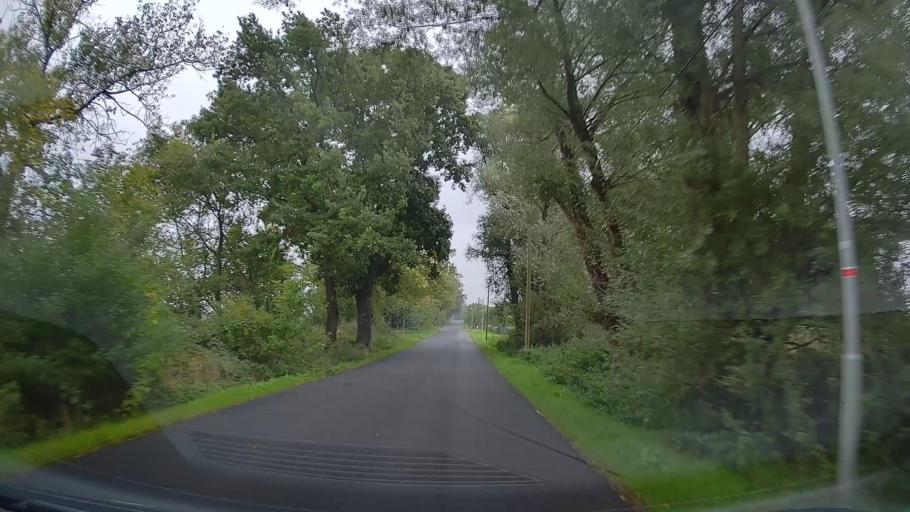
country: DE
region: Mecklenburg-Vorpommern
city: Hornstorf
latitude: 53.9234
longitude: 11.5392
